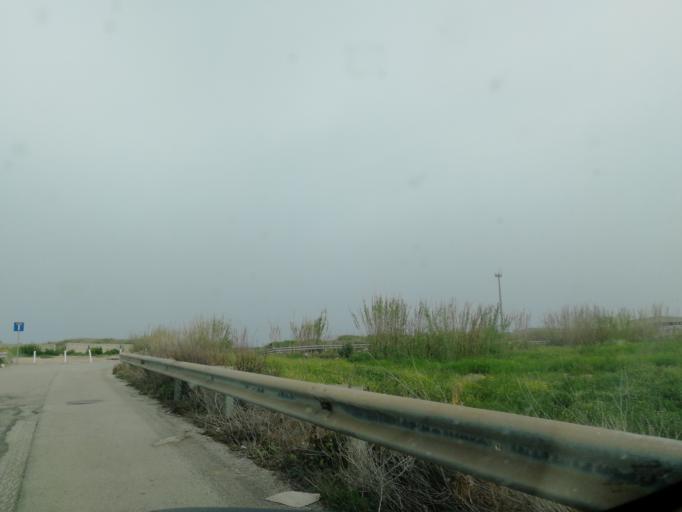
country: IT
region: Apulia
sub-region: Provincia di Barletta - Andria - Trani
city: Barletta
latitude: 41.3166
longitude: 16.3114
